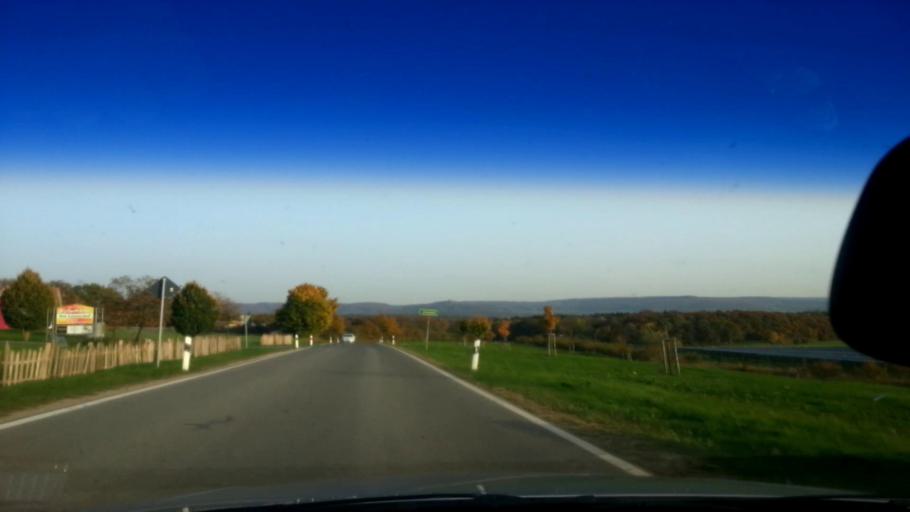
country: DE
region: Bavaria
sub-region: Upper Franconia
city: Zapfendorf
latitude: 49.9851
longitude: 10.9638
